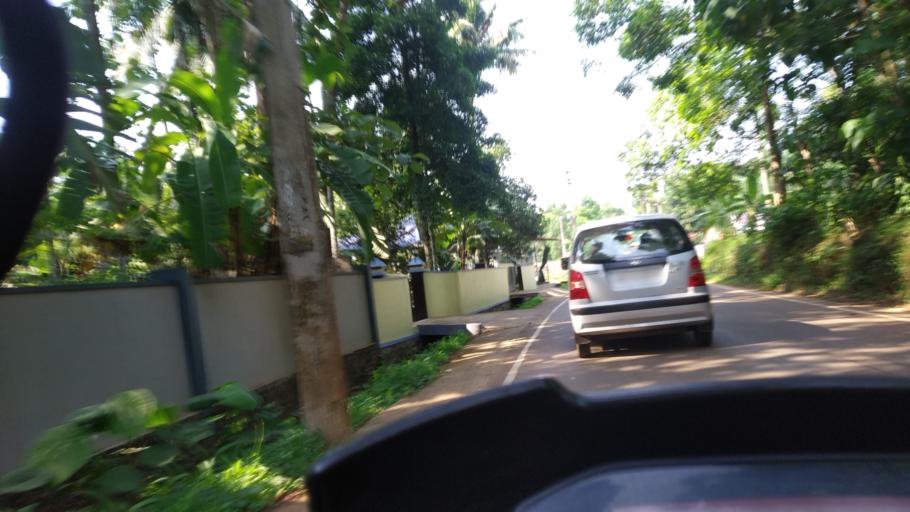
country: IN
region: Kerala
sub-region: Ernakulam
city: Piravam
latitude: 9.8426
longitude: 76.5357
